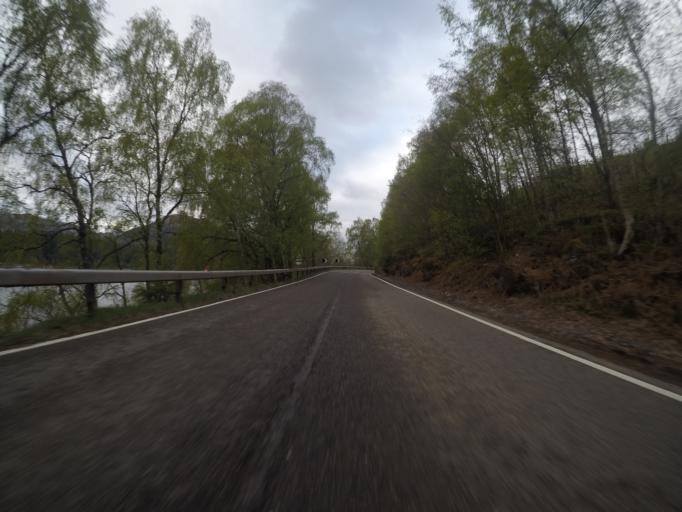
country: GB
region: Scotland
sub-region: Highland
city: Kingussie
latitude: 56.9594
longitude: -4.4629
